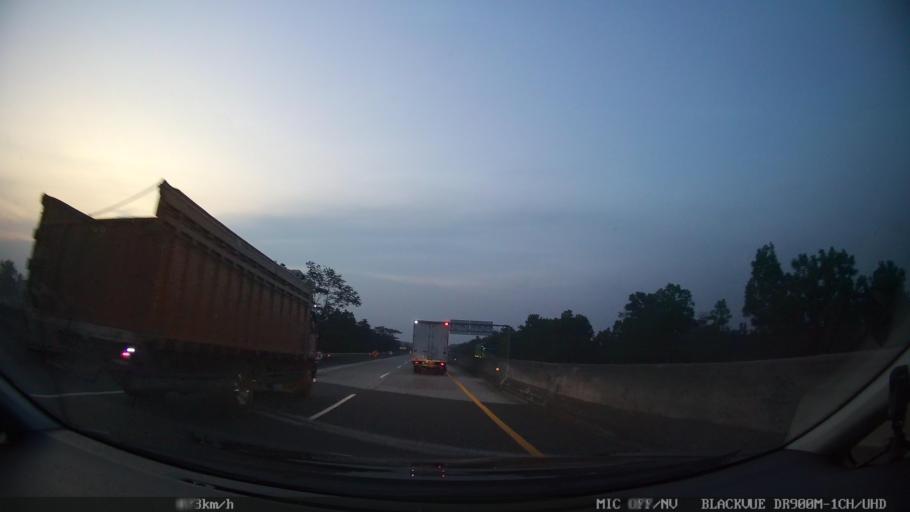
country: ID
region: Lampung
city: Sidorejo
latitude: -5.5680
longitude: 105.5367
